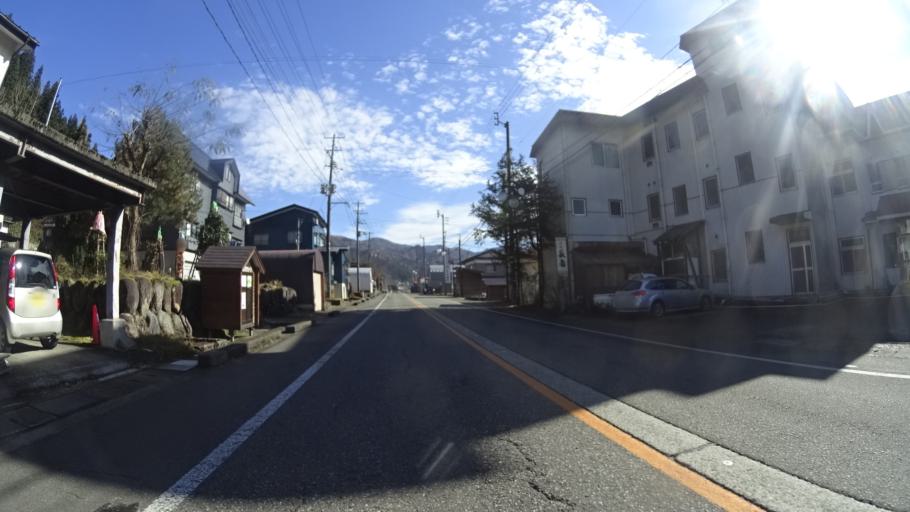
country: JP
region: Niigata
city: Muikamachi
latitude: 37.2080
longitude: 139.0627
